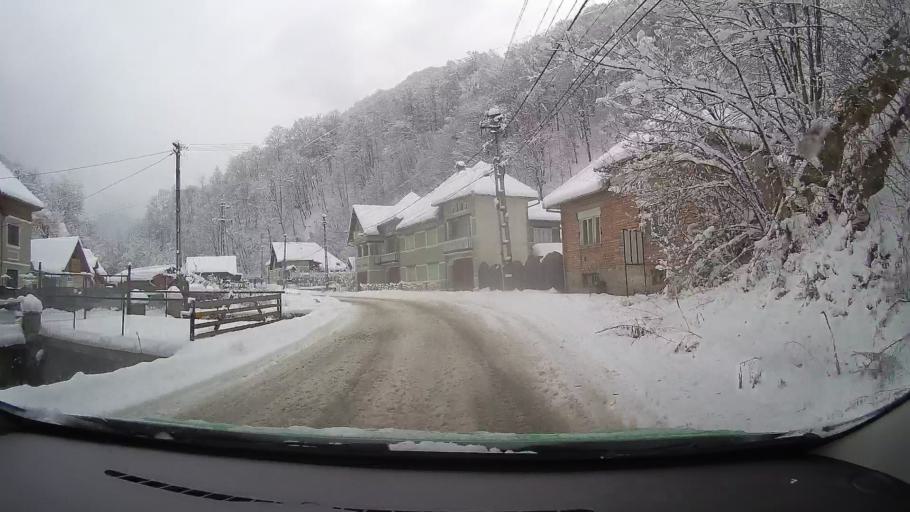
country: RO
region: Alba
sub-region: Comuna Sugag
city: Dobra
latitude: 45.7625
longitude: 23.6562
